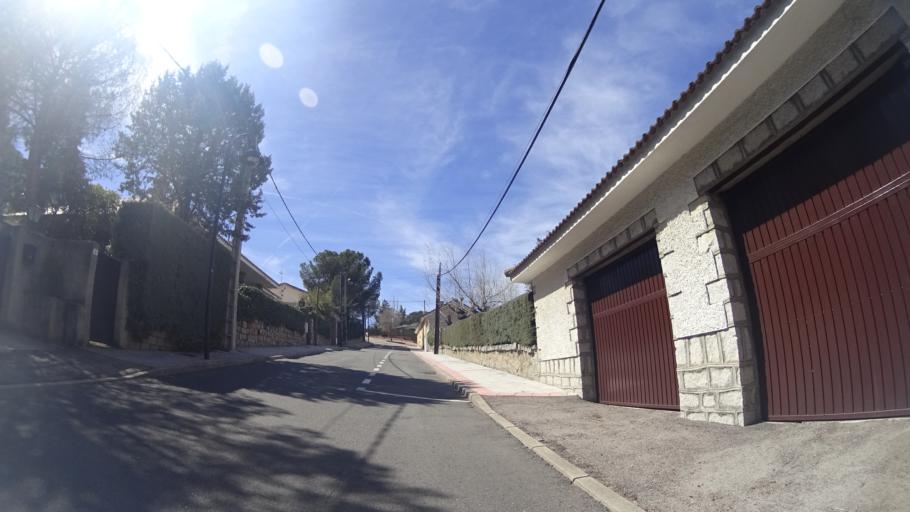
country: ES
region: Madrid
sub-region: Provincia de Madrid
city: Galapagar
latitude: 40.5929
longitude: -3.9853
